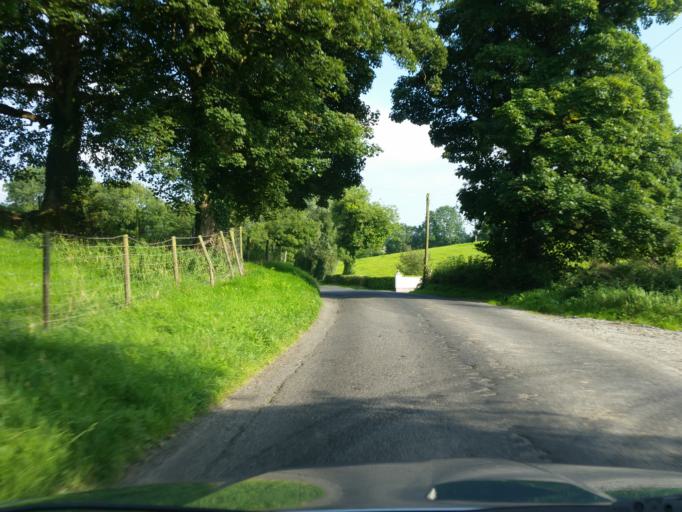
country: GB
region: Northern Ireland
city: Lisnaskea
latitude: 54.2849
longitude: -7.4382
